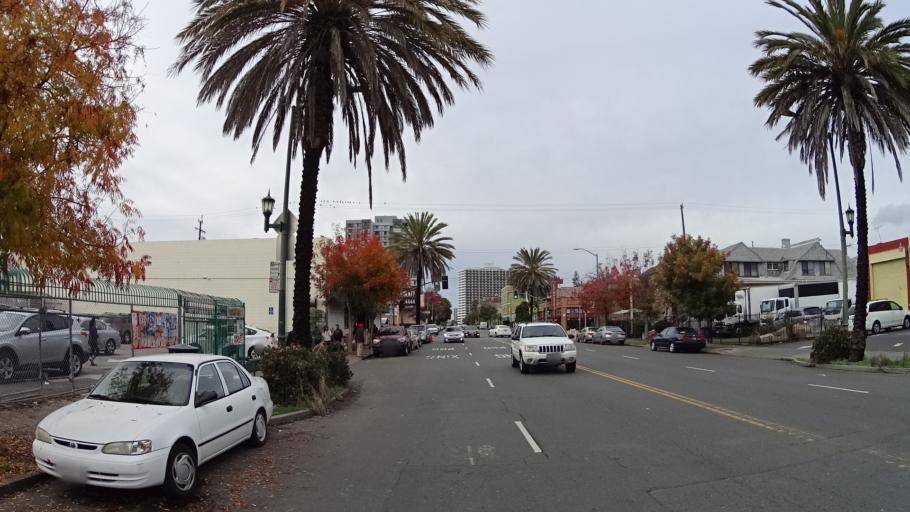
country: US
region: California
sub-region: Alameda County
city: Oakland
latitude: 37.7946
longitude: -122.2543
